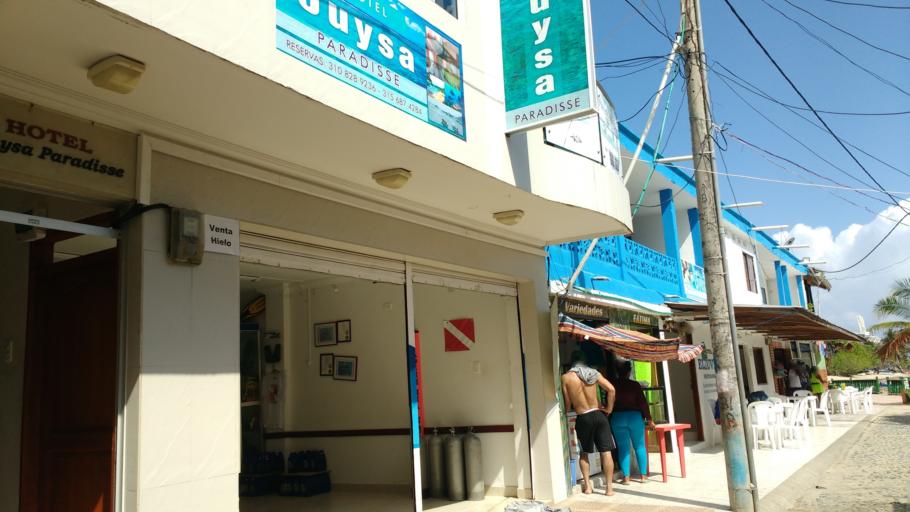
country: PA
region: Guna Yala
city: Puerto Obaldia
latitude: 8.6377
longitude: -77.3469
